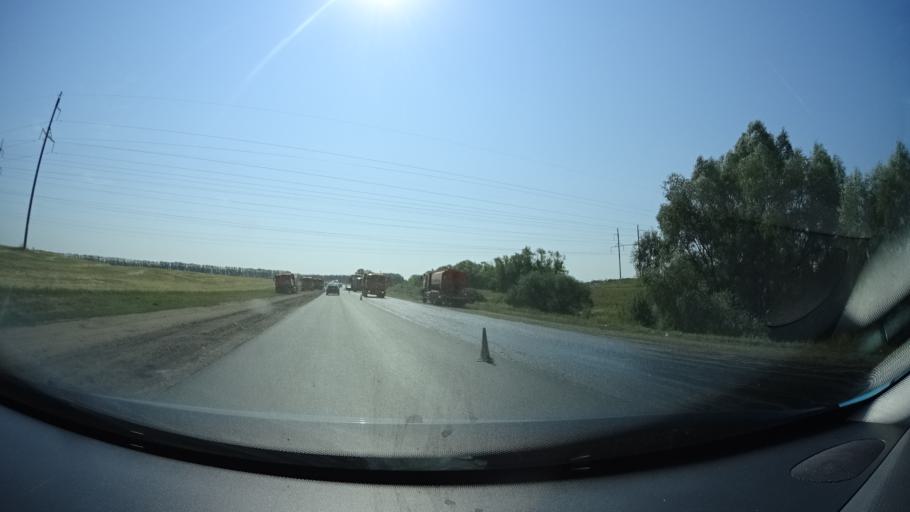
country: RU
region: Bashkortostan
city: Kabakovo
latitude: 54.4874
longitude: 55.9194
